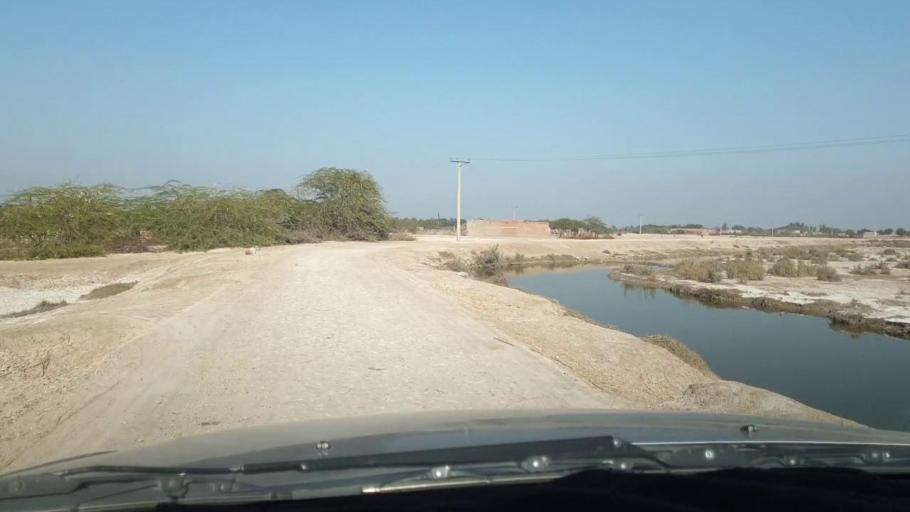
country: PK
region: Sindh
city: Mirpur Mathelo
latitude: 27.9752
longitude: 69.5604
